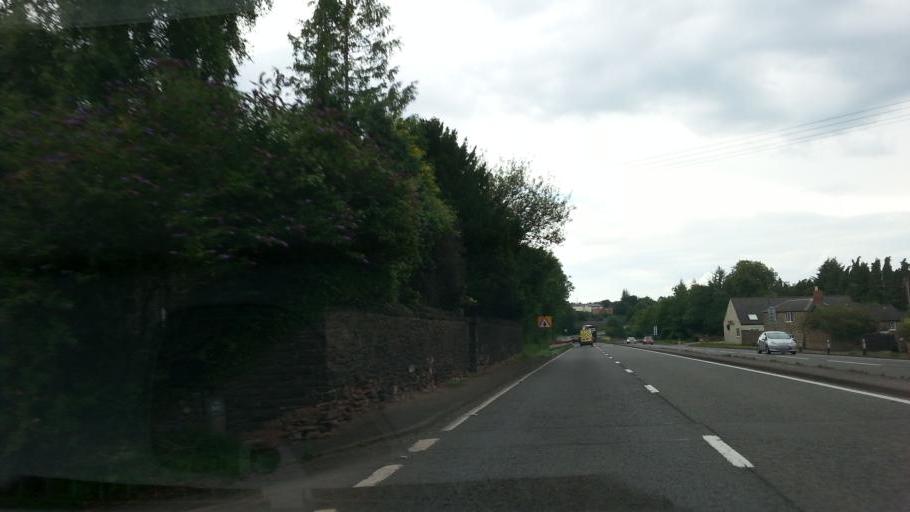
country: GB
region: England
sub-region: Herefordshire
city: Marstow
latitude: 51.8839
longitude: -2.6340
